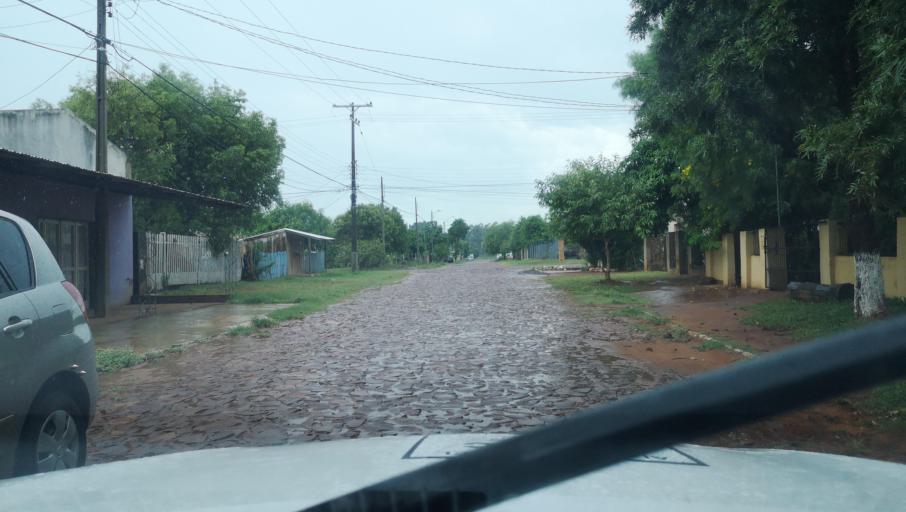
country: PY
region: Misiones
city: Santa Maria
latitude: -26.8954
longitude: -57.0322
